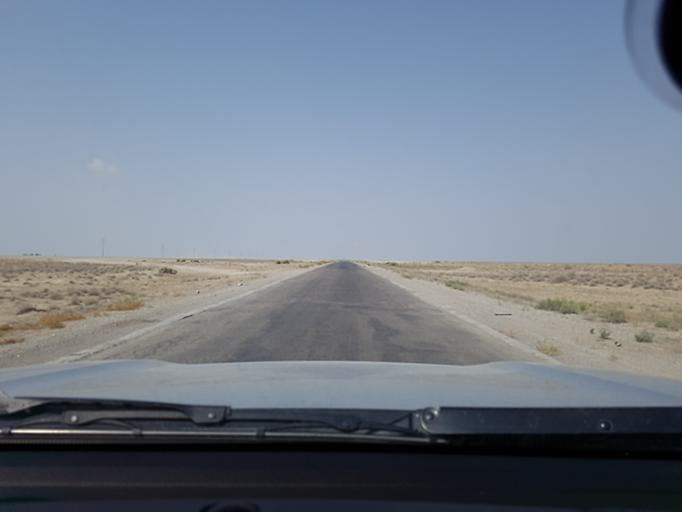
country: TM
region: Balkan
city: Gumdag
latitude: 38.7608
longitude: 54.5741
